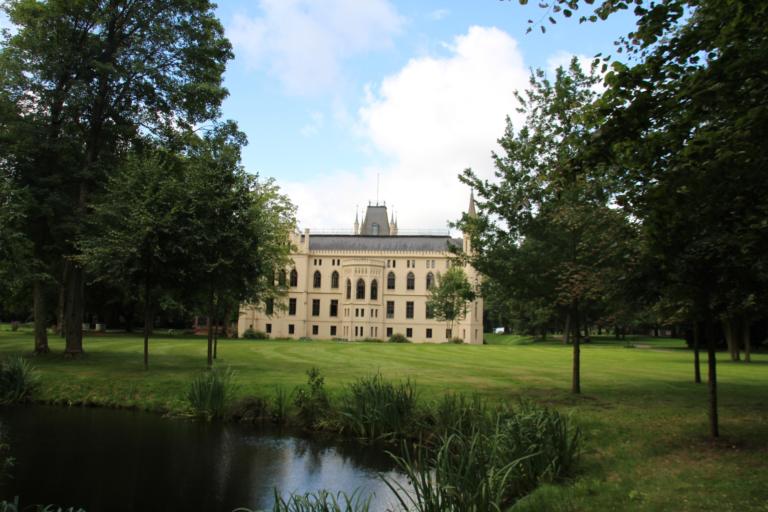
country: DE
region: Lower Saxony
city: Leer
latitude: 53.2310
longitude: 7.4947
